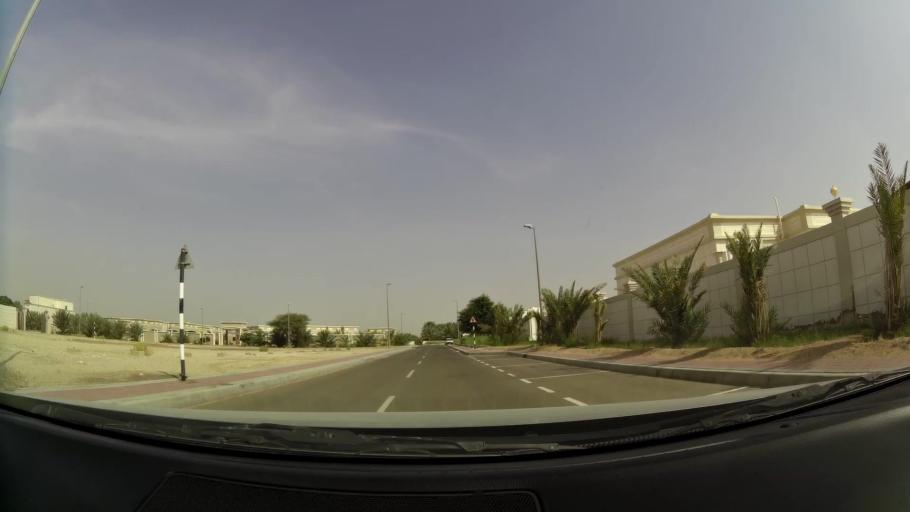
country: AE
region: Abu Dhabi
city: Al Ain
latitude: 24.1531
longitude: 55.7051
